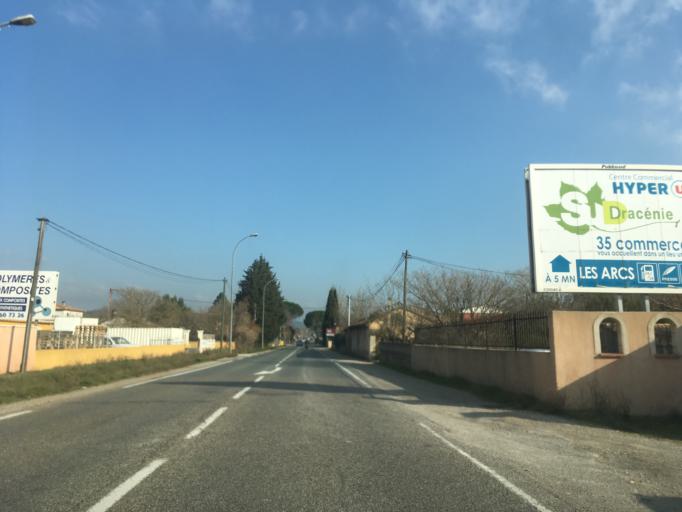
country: FR
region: Provence-Alpes-Cote d'Azur
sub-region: Departement du Var
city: Vidauban
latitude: 43.4161
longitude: 6.4206
